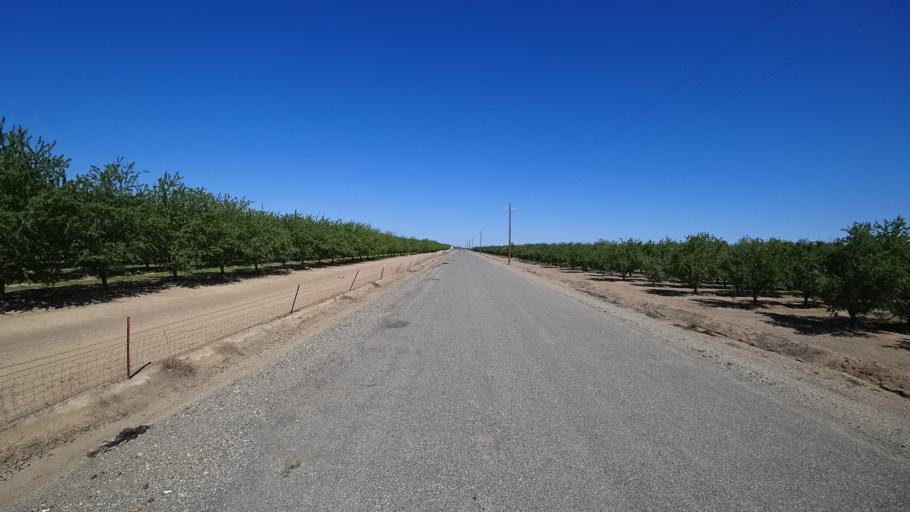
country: US
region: California
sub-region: Glenn County
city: Orland
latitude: 39.6412
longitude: -122.2347
